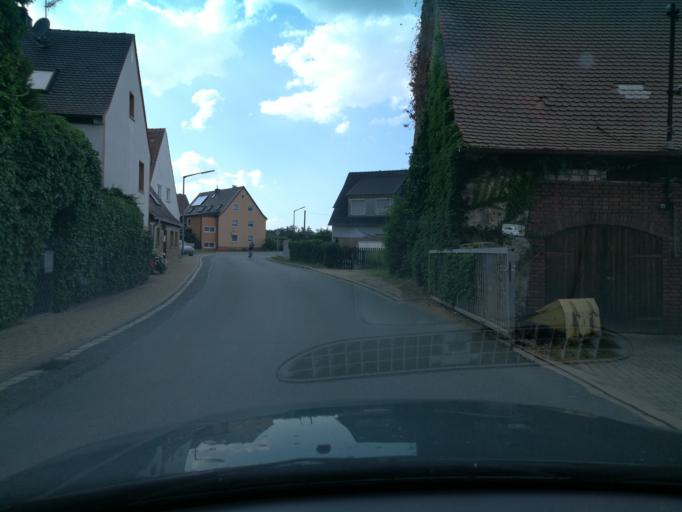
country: DE
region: Bavaria
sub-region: Regierungsbezirk Mittelfranken
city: Cadolzburg
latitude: 49.4849
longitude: 10.8506
